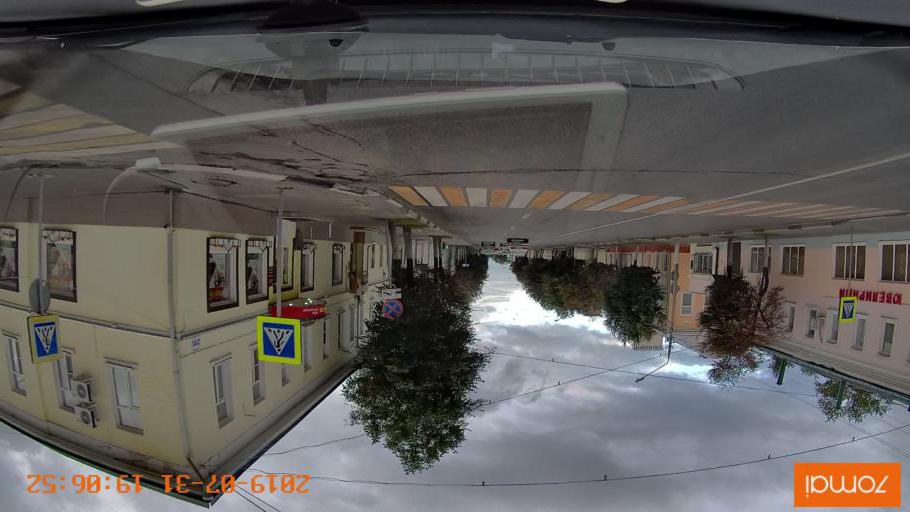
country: RU
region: Moskovskaya
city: Kolomna
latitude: 55.1001
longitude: 38.7572
